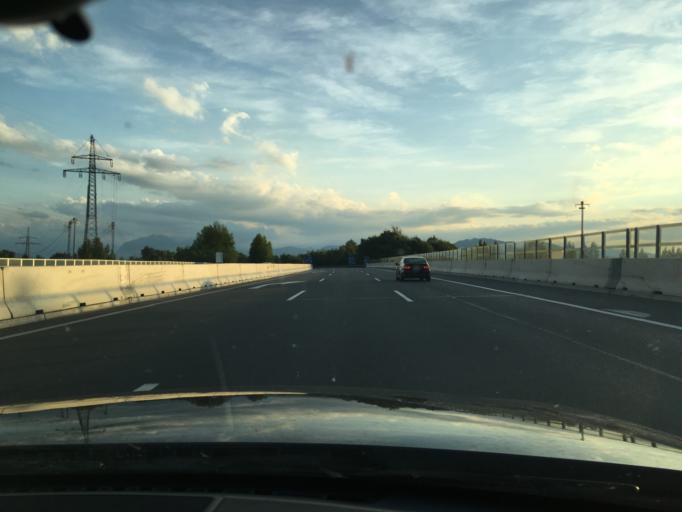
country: AT
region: Vorarlberg
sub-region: Politischer Bezirk Bregenz
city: Lauterach
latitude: 47.4634
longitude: 9.7295
